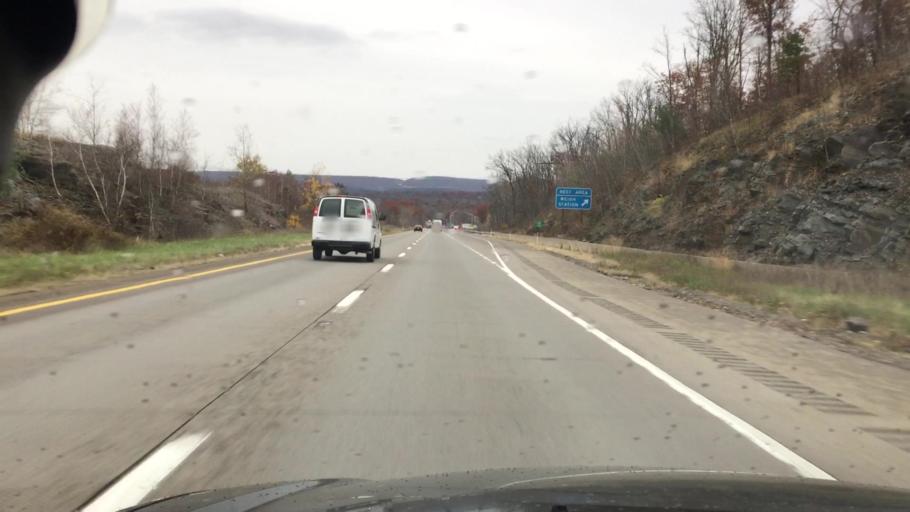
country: US
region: Pennsylvania
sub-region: Luzerne County
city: Freeland
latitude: 41.0951
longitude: -75.9617
